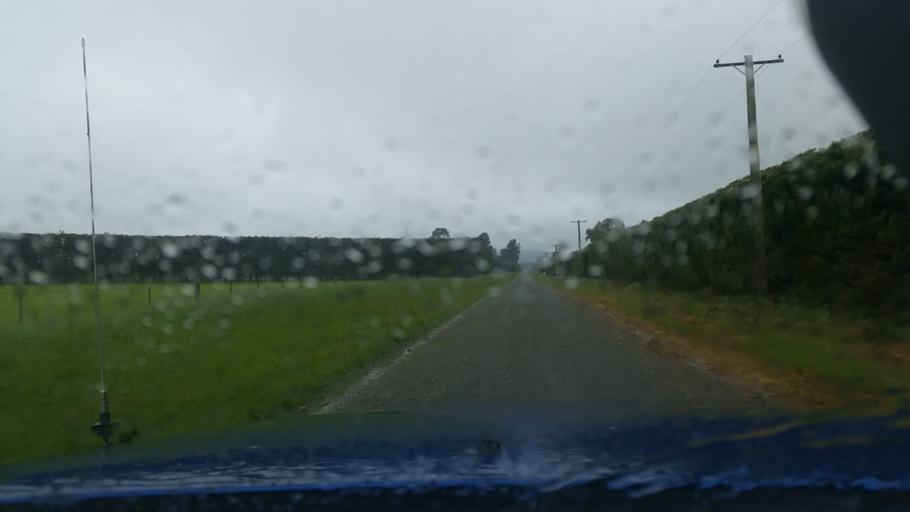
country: NZ
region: Canterbury
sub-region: Ashburton District
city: Methven
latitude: -43.7592
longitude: 171.2667
